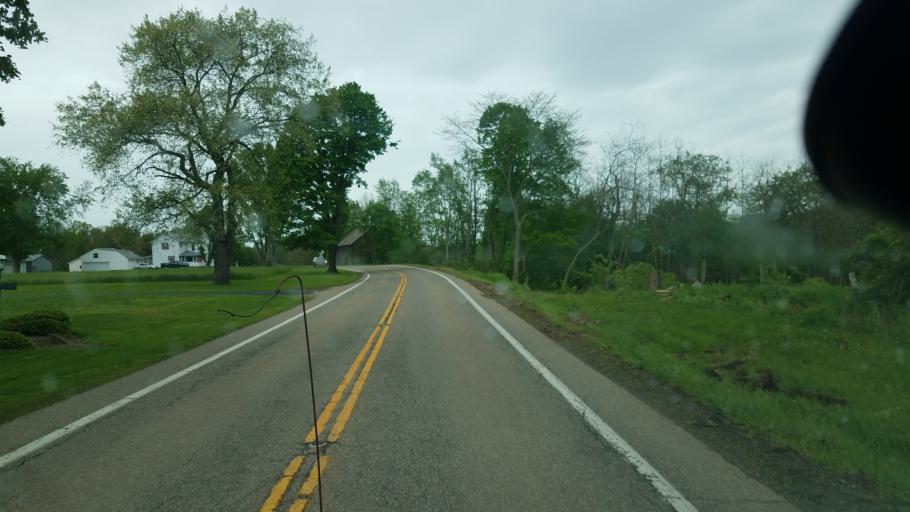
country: US
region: Ohio
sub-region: Coshocton County
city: West Lafayette
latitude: 40.2121
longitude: -81.7254
